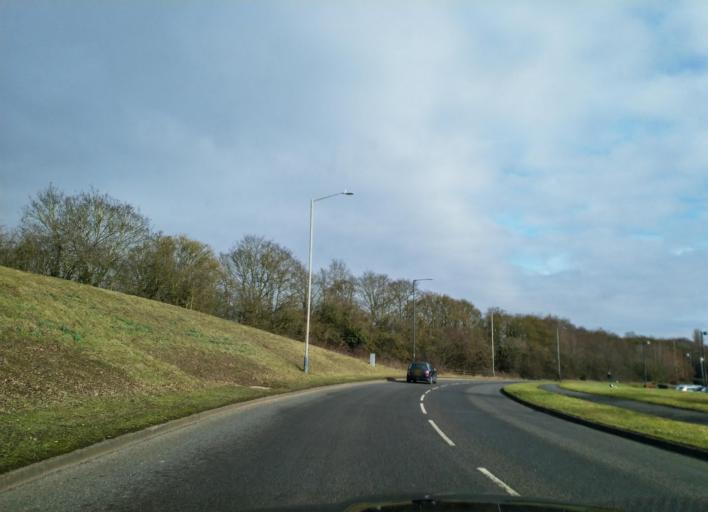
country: GB
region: England
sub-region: Warwickshire
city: Warwick
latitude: 52.2948
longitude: -1.6003
